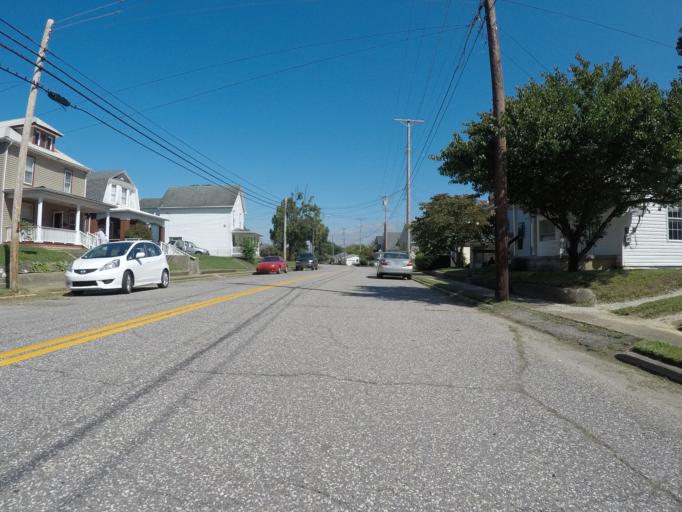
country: US
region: Kentucky
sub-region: Boyd County
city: Catlettsburg
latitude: 38.4085
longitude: -82.5986
